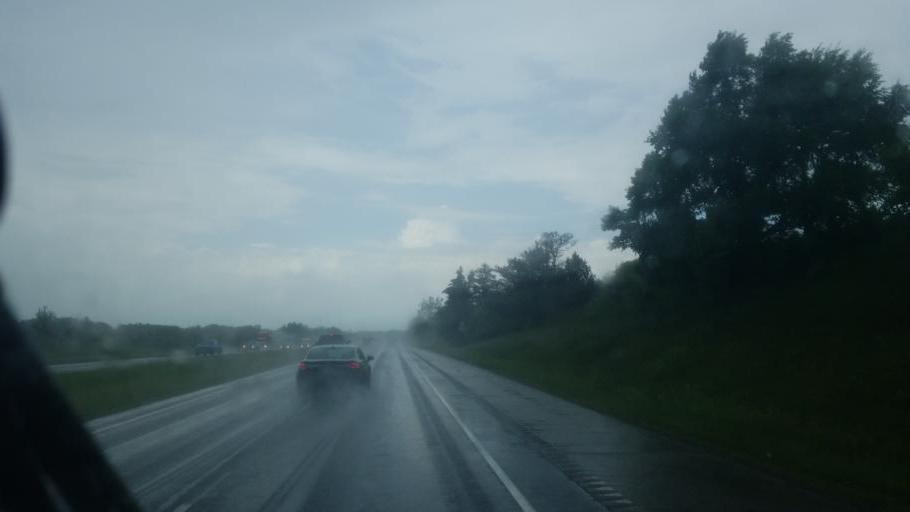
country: US
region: Indiana
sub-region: Whitley County
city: Columbia City
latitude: 41.1581
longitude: -85.4609
